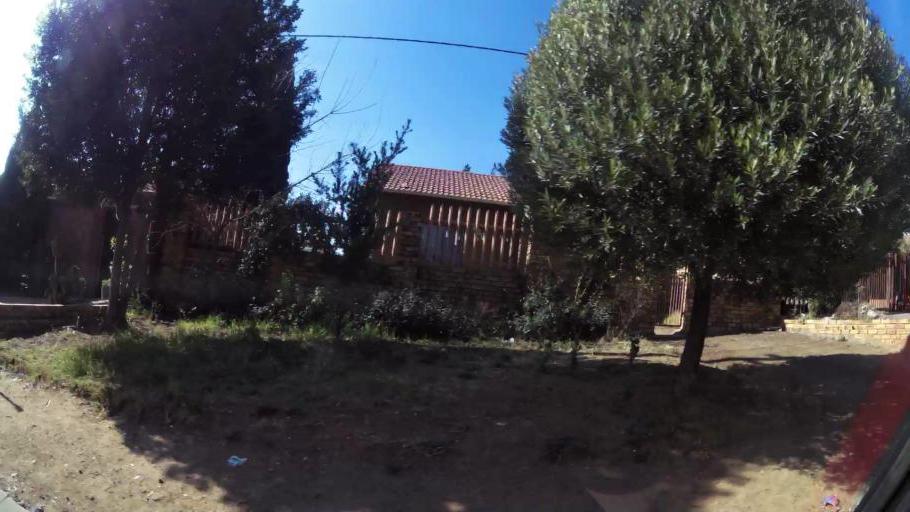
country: ZA
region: Gauteng
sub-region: West Rand District Municipality
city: Muldersdriseloop
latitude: -26.0146
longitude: 27.9356
